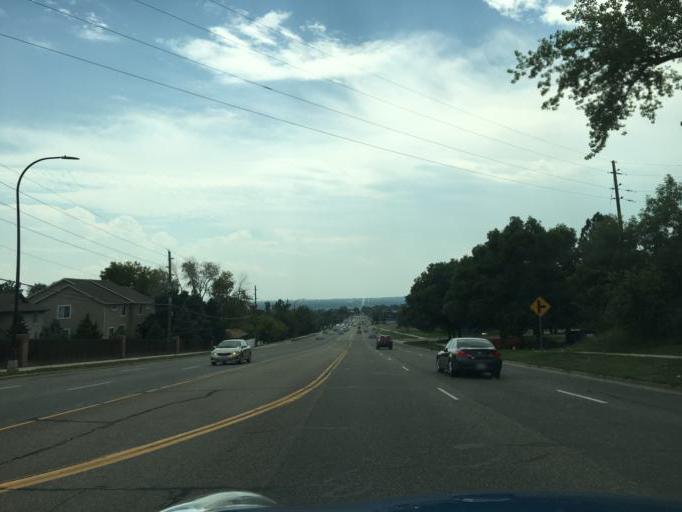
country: US
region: Colorado
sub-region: Jefferson County
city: Arvada
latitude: 39.8252
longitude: -105.0815
